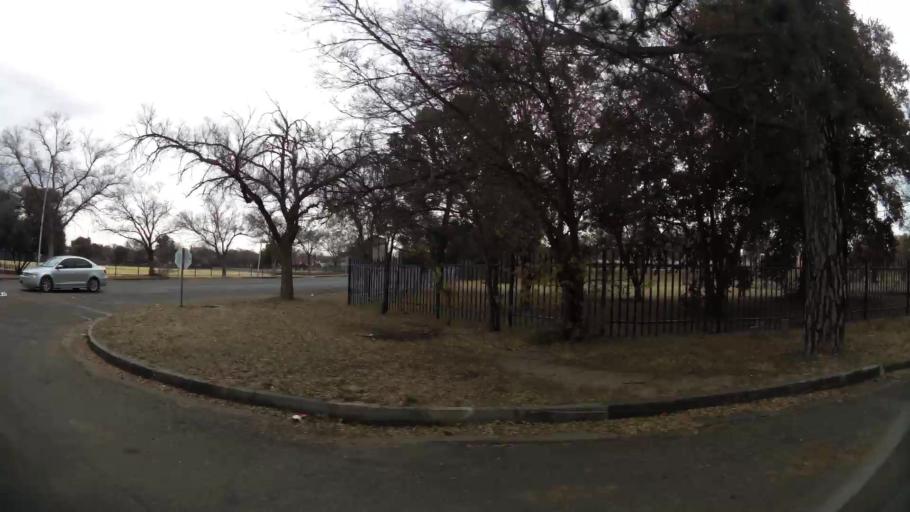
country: ZA
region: Orange Free State
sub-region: Fezile Dabi District Municipality
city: Kroonstad
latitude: -27.6613
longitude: 27.2449
